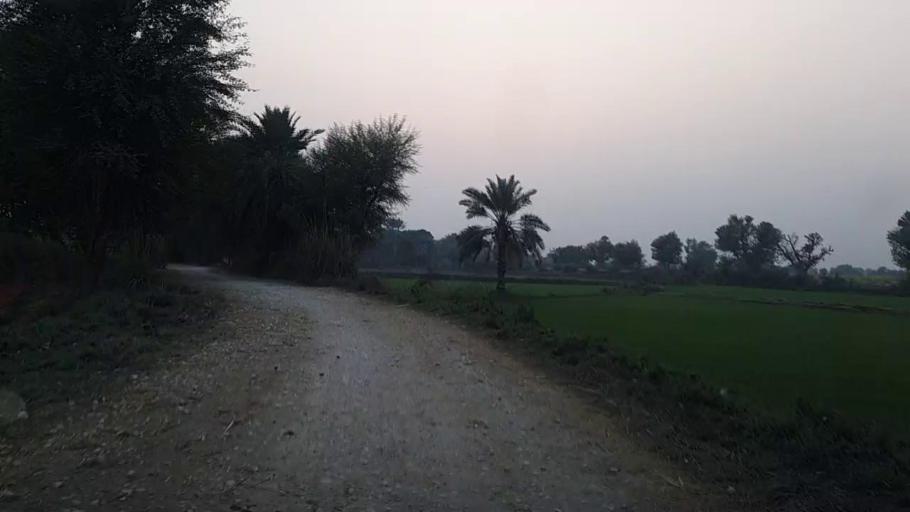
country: PK
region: Sindh
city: Kandiari
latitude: 26.9827
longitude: 68.4953
